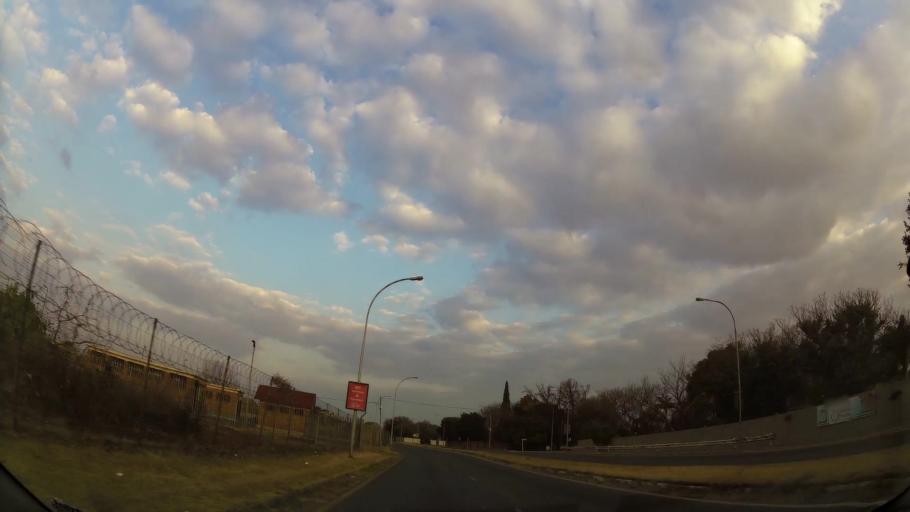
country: ZA
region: Gauteng
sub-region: Ekurhuleni Metropolitan Municipality
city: Benoni
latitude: -26.1645
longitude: 28.3074
